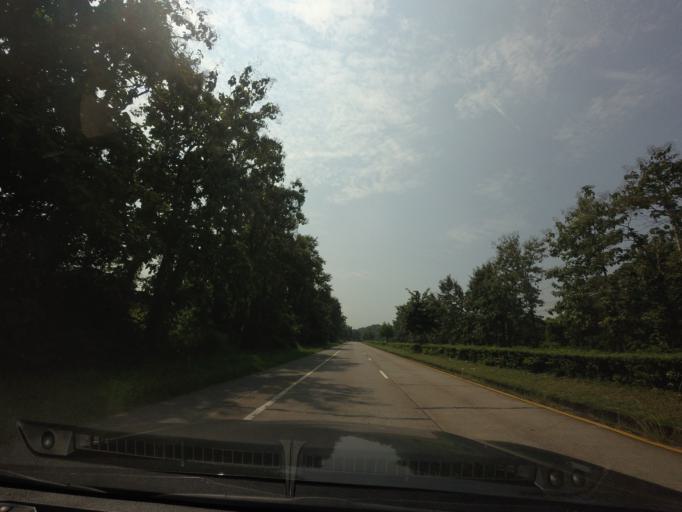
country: TH
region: Phrae
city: Sung Men
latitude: 18.0020
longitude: 100.1036
